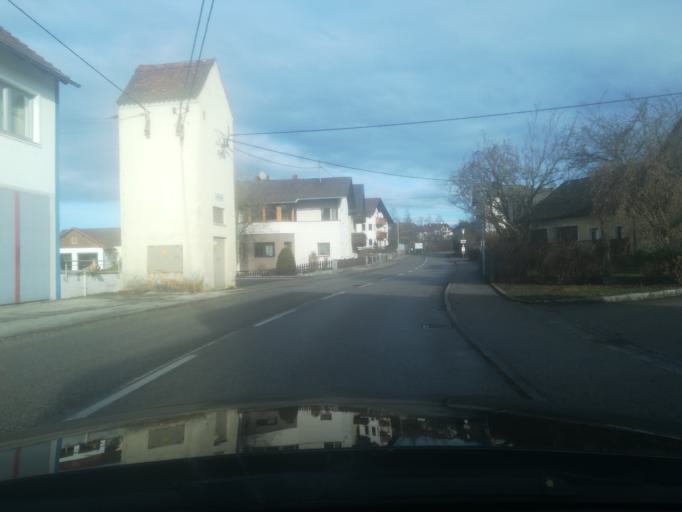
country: AT
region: Upper Austria
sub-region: Politischer Bezirk Perg
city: Perg
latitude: 48.3342
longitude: 14.6215
